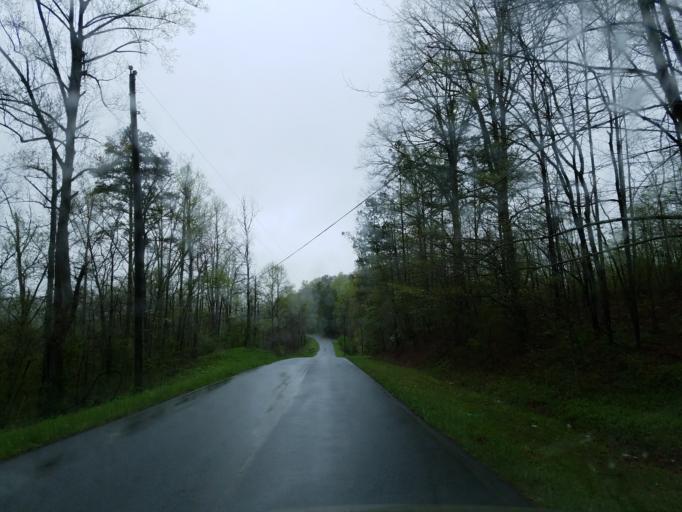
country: US
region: Georgia
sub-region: Gilmer County
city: Ellijay
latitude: 34.5665
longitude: -84.5295
